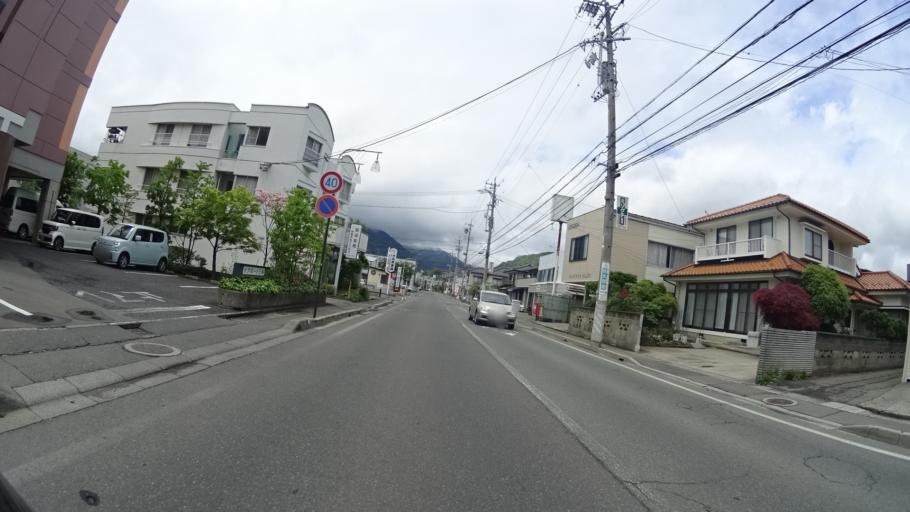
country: JP
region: Nagano
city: Nagano-shi
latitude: 36.6590
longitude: 138.2021
